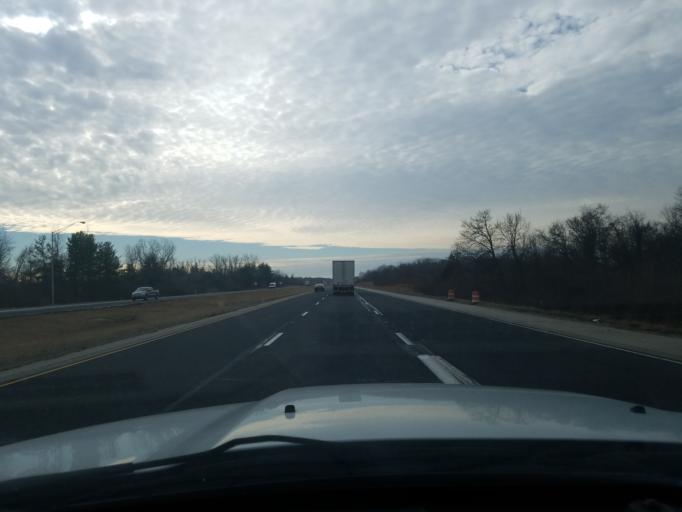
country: US
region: Indiana
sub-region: Huntington County
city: Markle
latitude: 40.8254
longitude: -85.3567
